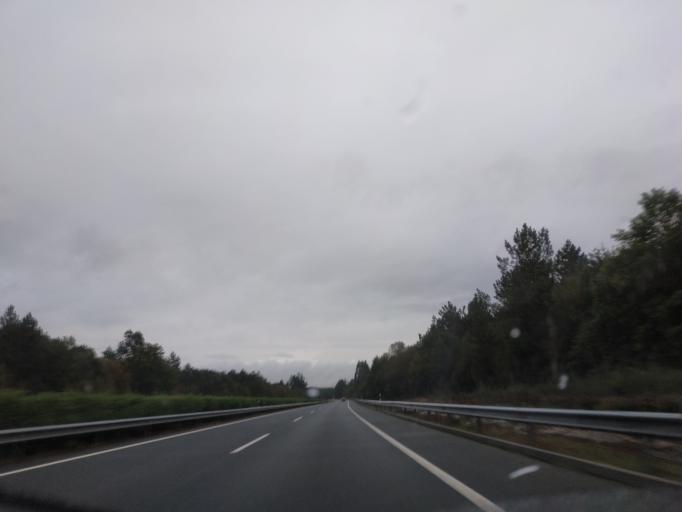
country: ES
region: Galicia
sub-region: Provincia de Lugo
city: Begonte
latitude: 43.1478
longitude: -7.6563
